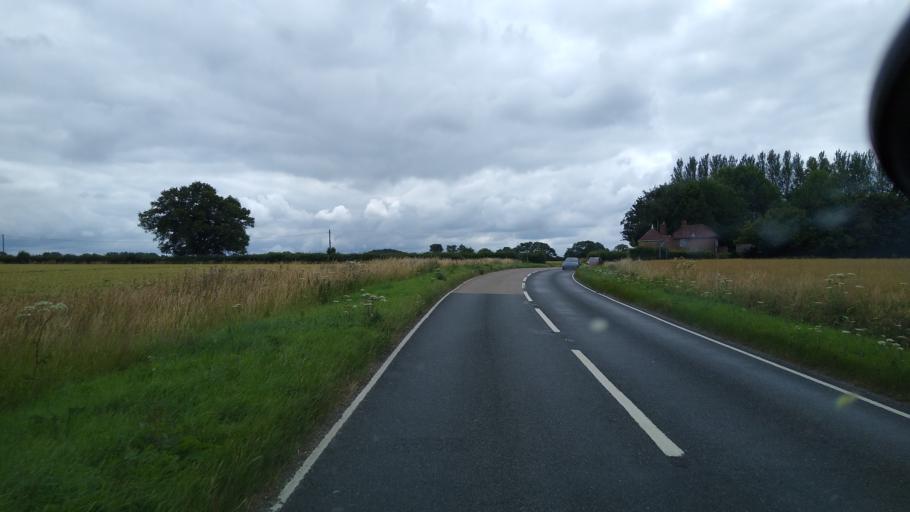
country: GB
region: England
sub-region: Hampshire
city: Alton
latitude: 51.1250
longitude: -0.9524
